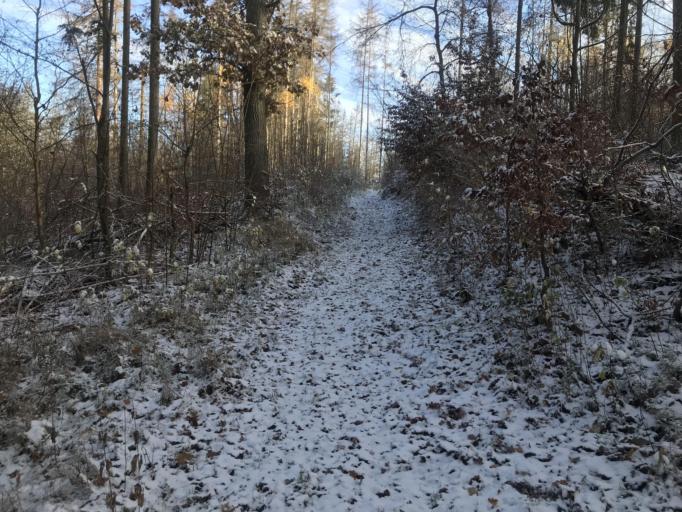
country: DE
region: Saxony-Anhalt
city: Harzgerode
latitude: 51.6035
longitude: 11.1311
